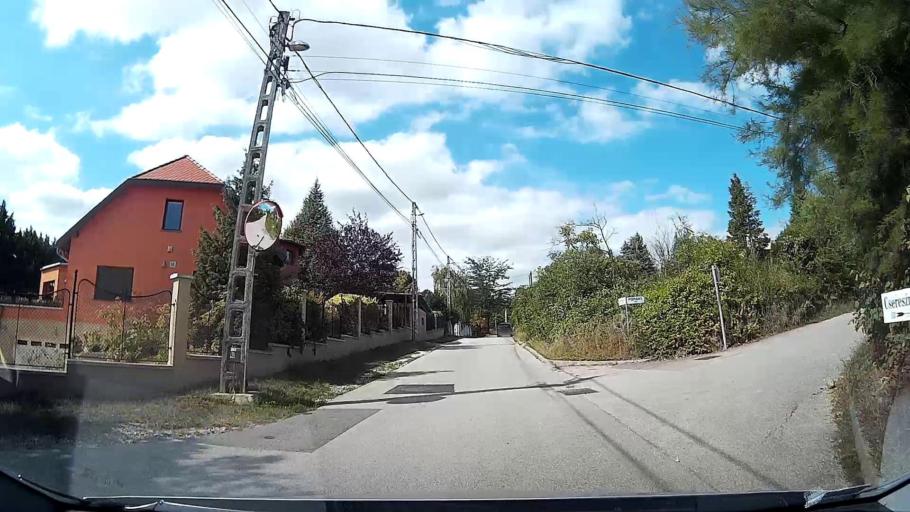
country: HU
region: Pest
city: Szentendre
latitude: 47.6859
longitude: 19.0742
